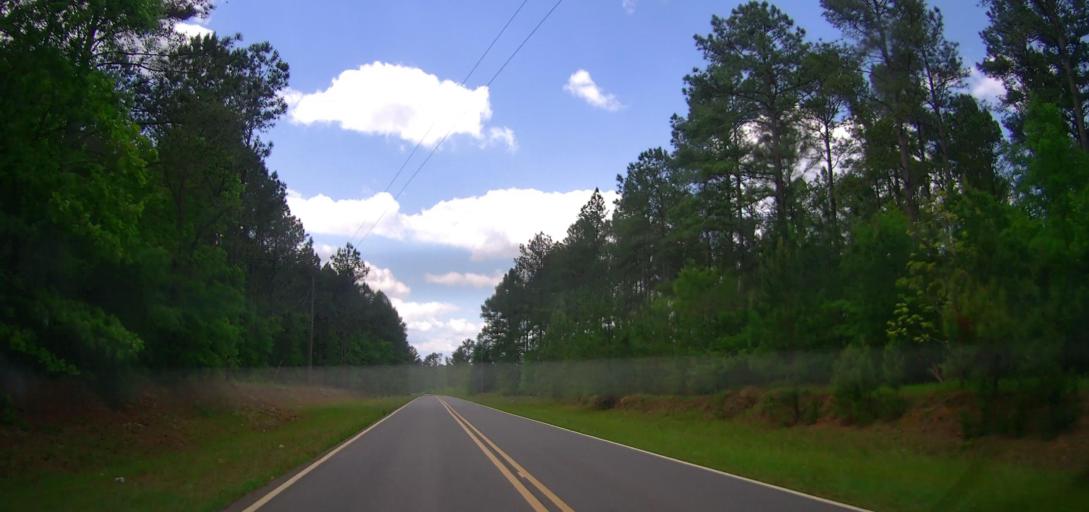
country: US
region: Georgia
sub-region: Laurens County
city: East Dublin
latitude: 32.6185
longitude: -82.8173
